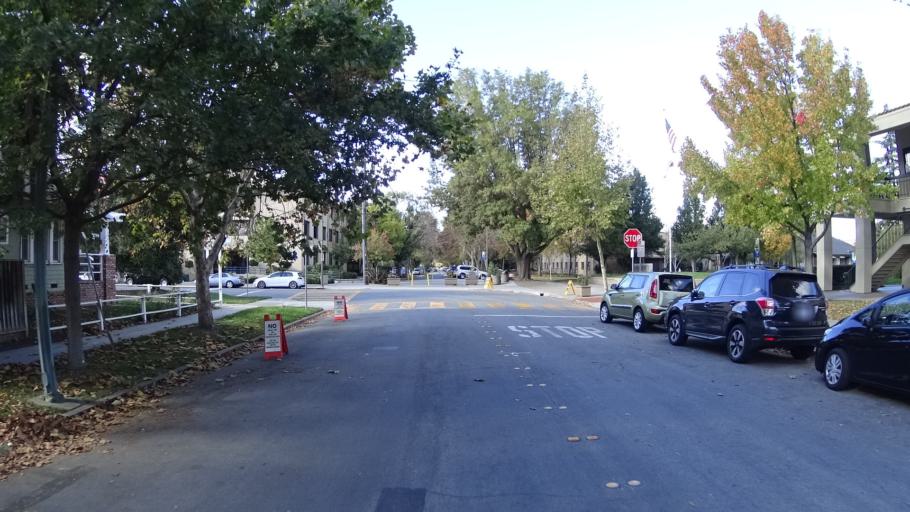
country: US
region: California
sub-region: Santa Clara County
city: Buena Vista
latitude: 37.3415
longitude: -121.9189
